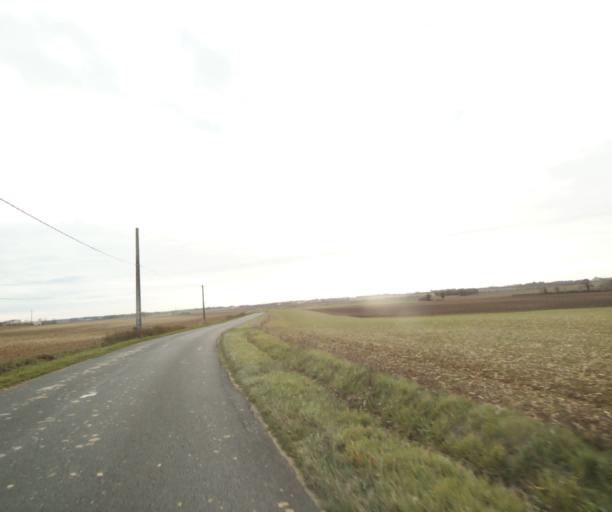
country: FR
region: Poitou-Charentes
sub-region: Departement de la Charente-Maritime
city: Corme-Royal
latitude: 45.7363
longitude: -0.8142
